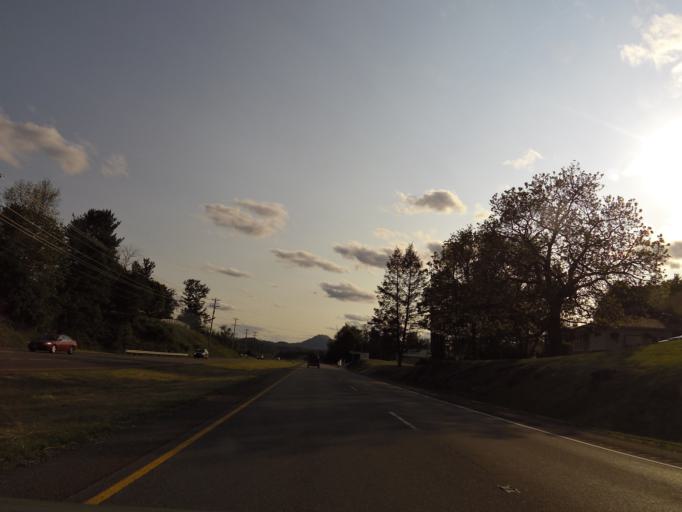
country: US
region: Virginia
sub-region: Tazewell County
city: Claypool Hill
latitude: 37.0563
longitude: -81.7660
